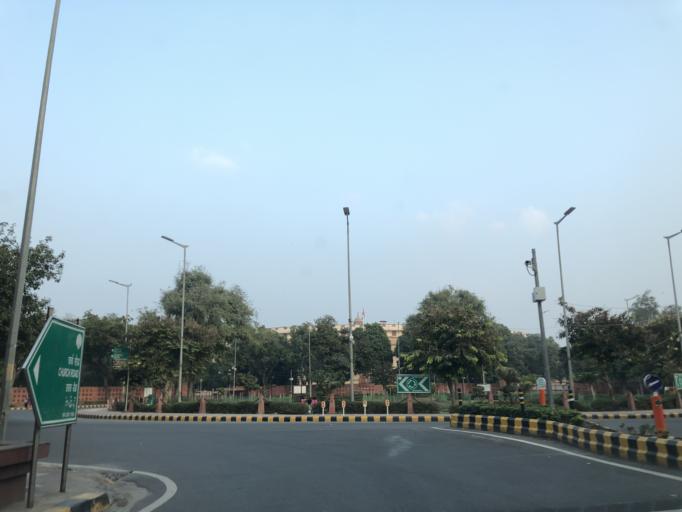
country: IN
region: NCT
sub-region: New Delhi
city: New Delhi
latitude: 28.6174
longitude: 77.2055
